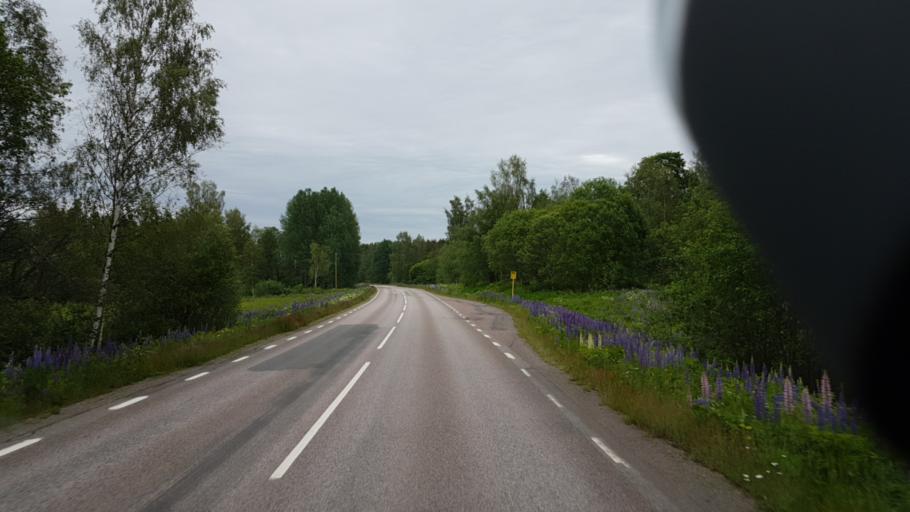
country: SE
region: Vaermland
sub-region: Eda Kommun
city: Amotfors
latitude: 59.6844
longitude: 12.3636
